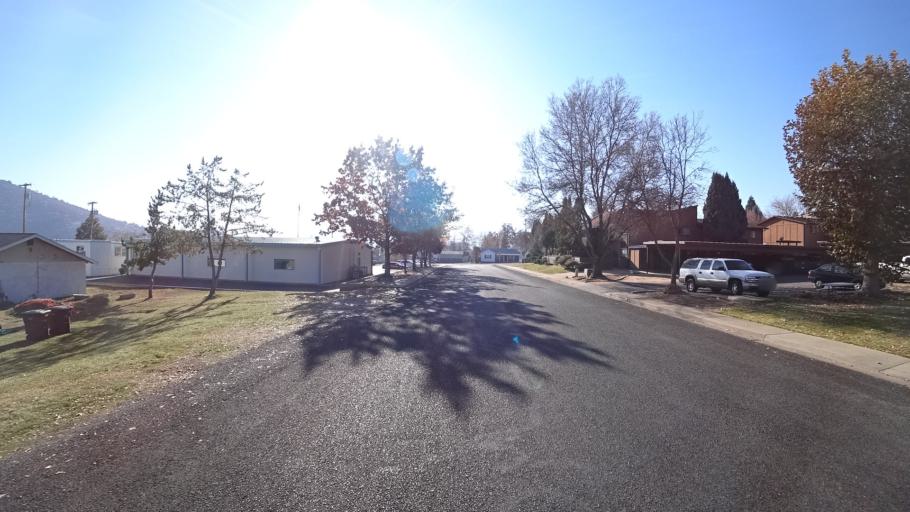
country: US
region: California
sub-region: Siskiyou County
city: Yreka
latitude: 41.7249
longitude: -122.6456
